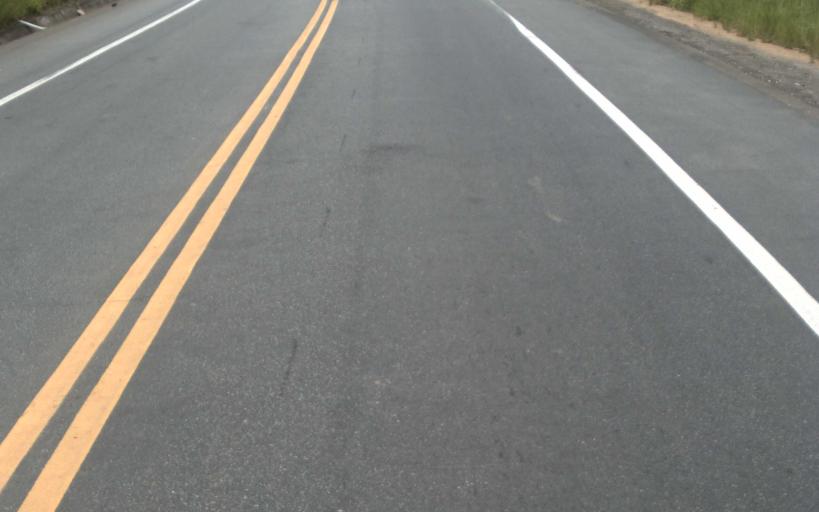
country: BR
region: Minas Gerais
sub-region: Coronel Fabriciano
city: Coronel Fabriciano
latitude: -19.5354
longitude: -42.5915
